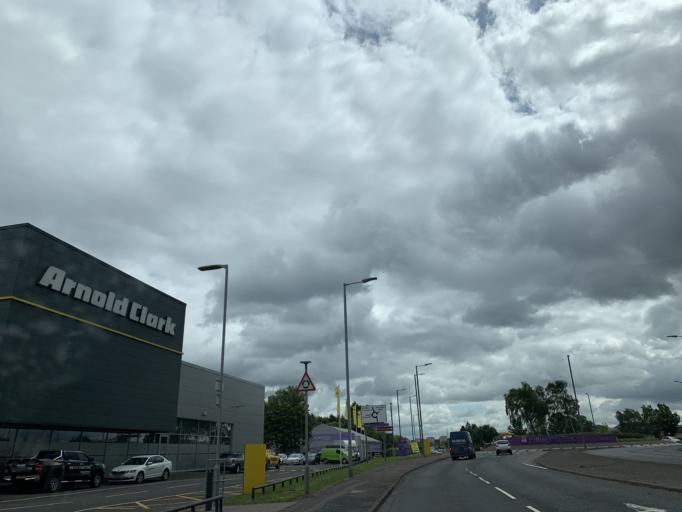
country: GB
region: Scotland
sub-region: Renfrewshire
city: Renfrew
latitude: 55.8638
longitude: -4.3651
